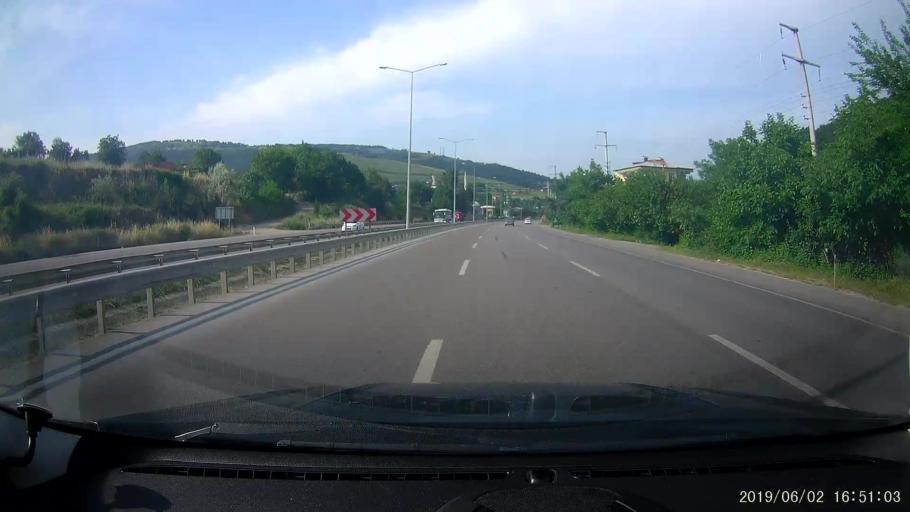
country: TR
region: Samsun
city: Taflan
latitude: 41.2675
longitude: 36.1776
